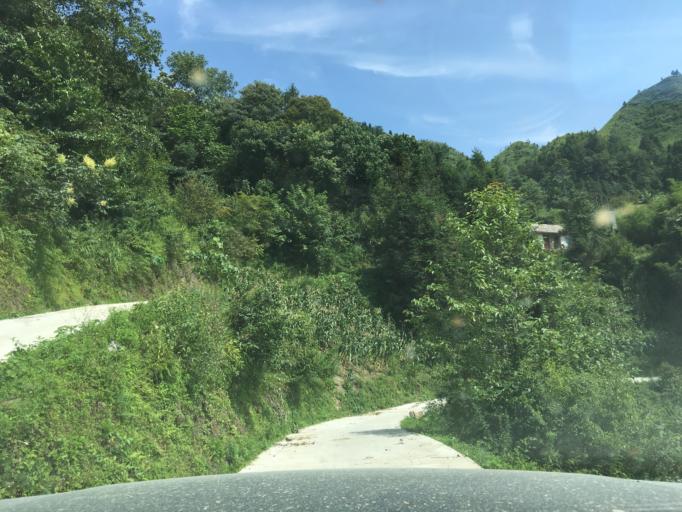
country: CN
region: Guangxi Zhuangzu Zizhiqu
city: Xinzhou
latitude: 24.9706
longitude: 105.6217
